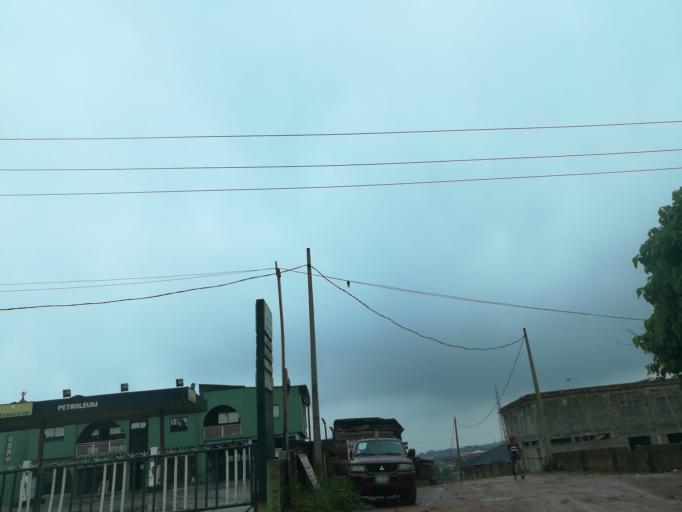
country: NG
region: Lagos
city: Ikorodu
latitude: 6.6411
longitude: 3.5153
